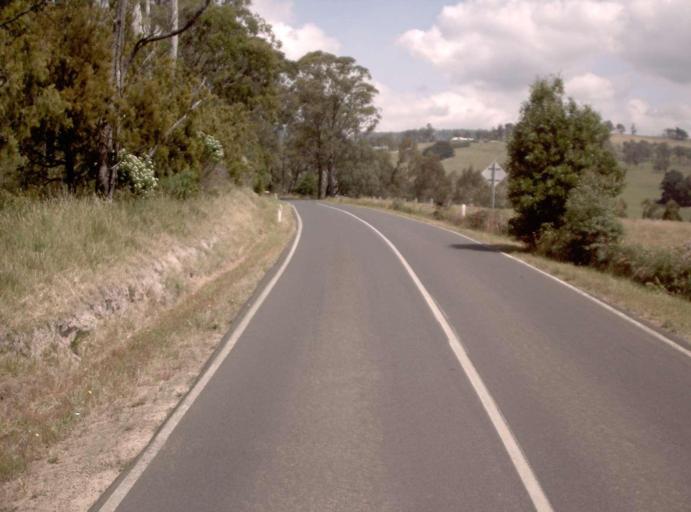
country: AU
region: Victoria
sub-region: Latrobe
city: Traralgon
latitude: -38.3024
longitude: 146.5392
